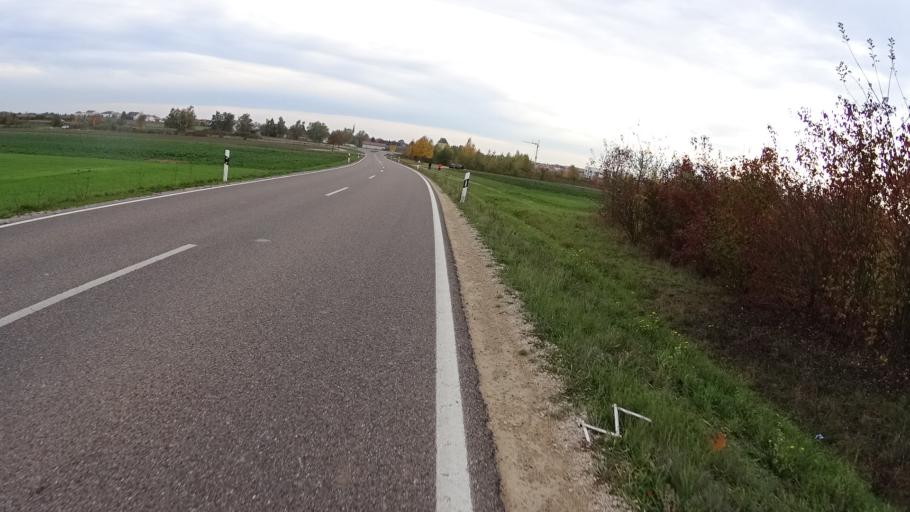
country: DE
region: Bavaria
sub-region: Upper Bavaria
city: Eitensheim
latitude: 48.8314
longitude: 11.3184
